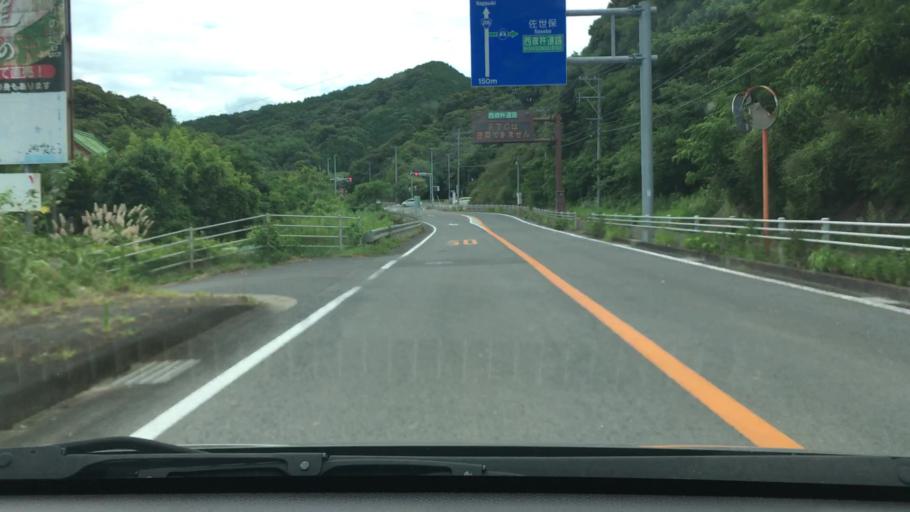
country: JP
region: Nagasaki
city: Sasebo
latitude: 32.9979
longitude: 129.7321
